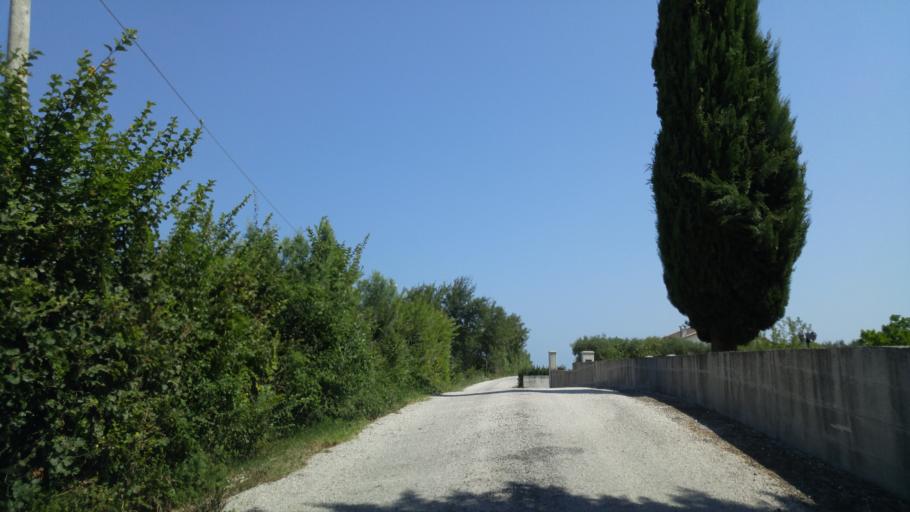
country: IT
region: The Marches
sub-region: Provincia di Pesaro e Urbino
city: Piagge
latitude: 43.7575
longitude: 12.9761
